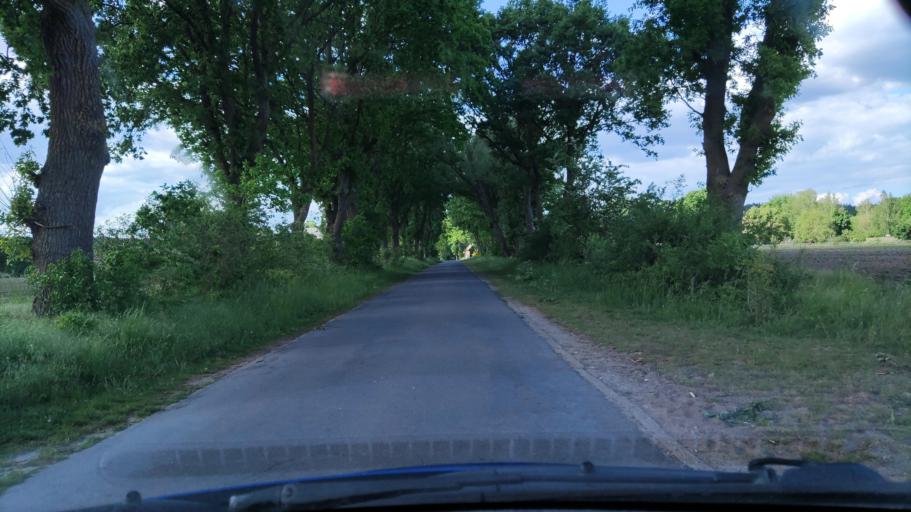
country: DE
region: Lower Saxony
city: Hitzacker
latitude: 53.1457
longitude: 10.9871
